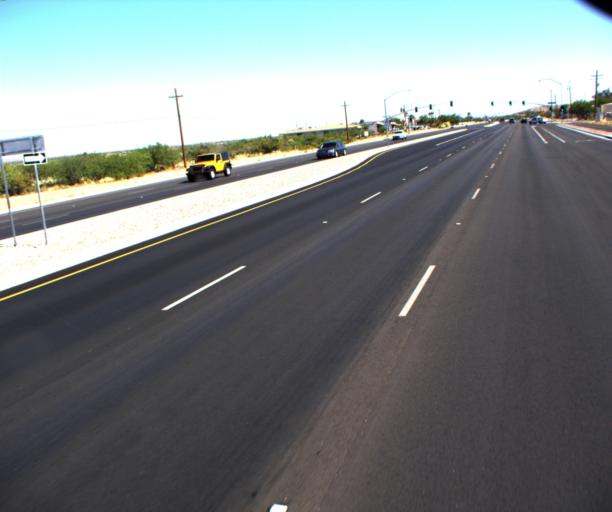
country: US
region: Arizona
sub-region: Pima County
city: Catalina
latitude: 32.5057
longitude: -110.9258
